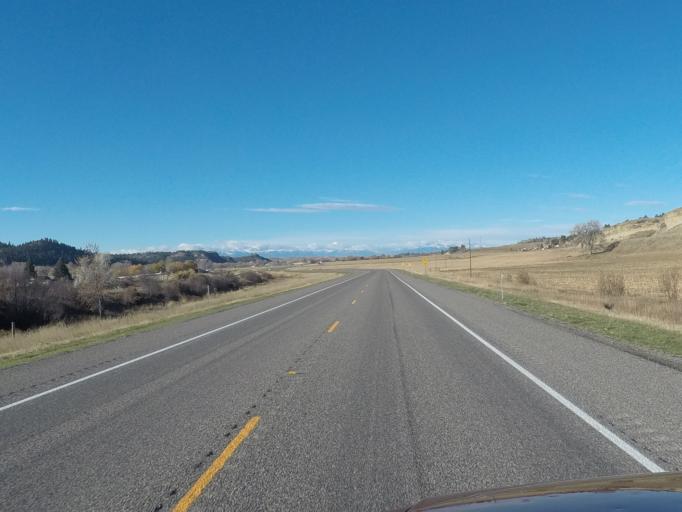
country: US
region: Montana
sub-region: Yellowstone County
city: Laurel
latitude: 45.4960
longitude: -108.9447
